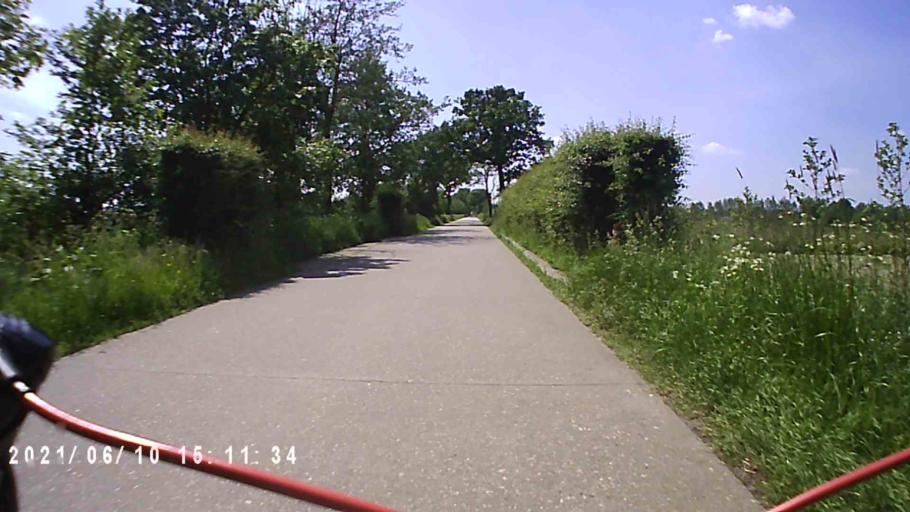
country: NL
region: Friesland
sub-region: Gemeente Achtkarspelen
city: Surhuizum
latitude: 53.2000
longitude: 6.1937
